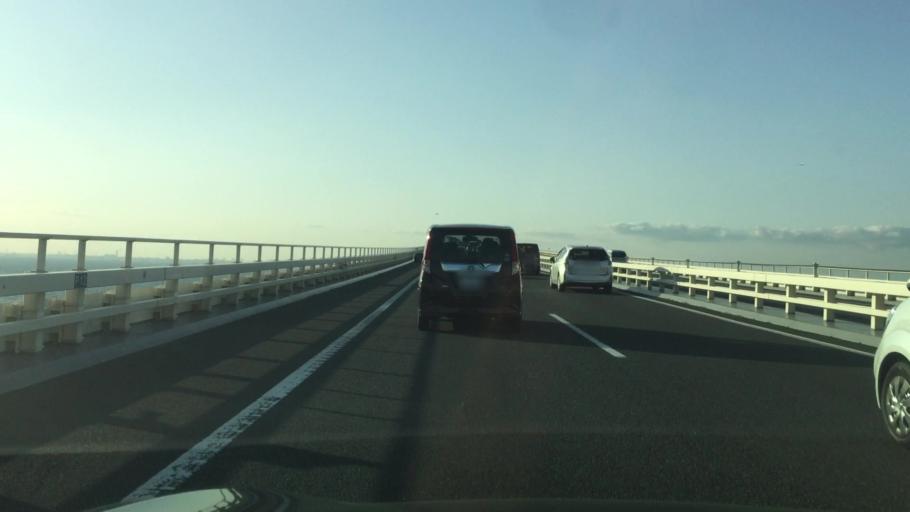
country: JP
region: Chiba
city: Kisarazu
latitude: 35.4508
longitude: 139.8944
